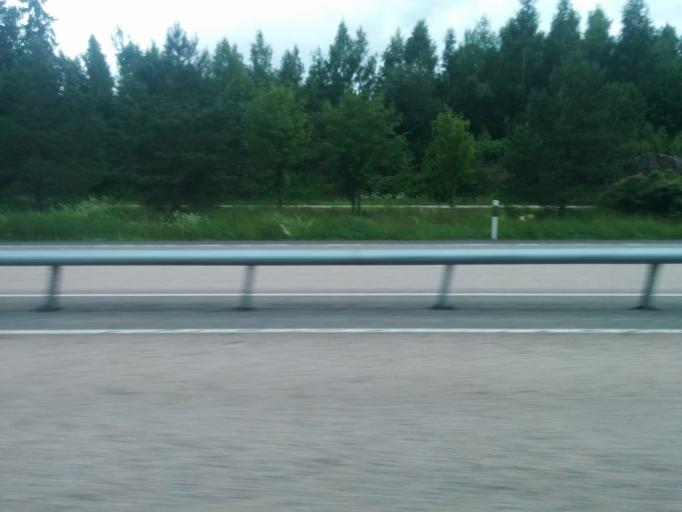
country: FI
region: Pirkanmaa
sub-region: Tampere
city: Orivesi
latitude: 61.7092
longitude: 24.5351
